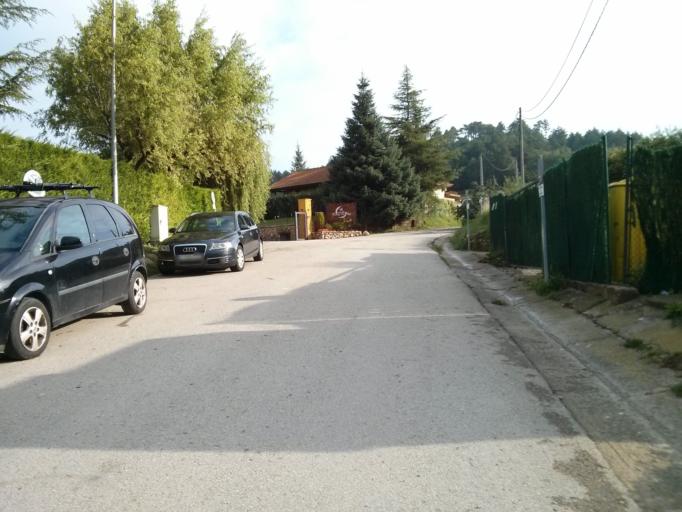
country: ES
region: Catalonia
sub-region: Provincia de Barcelona
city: Borreda
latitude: 42.0923
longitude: 2.0084
